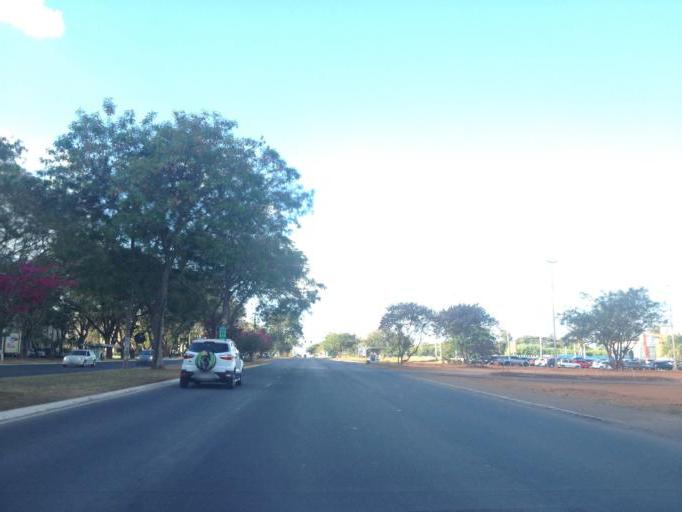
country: BR
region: Federal District
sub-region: Brasilia
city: Brasilia
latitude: -15.8338
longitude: -47.9129
